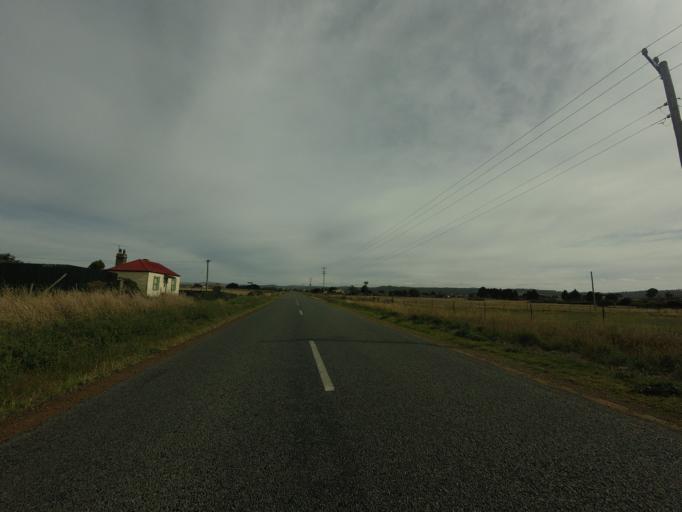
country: AU
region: Tasmania
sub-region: Brighton
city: Bridgewater
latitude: -42.3181
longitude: 147.3758
